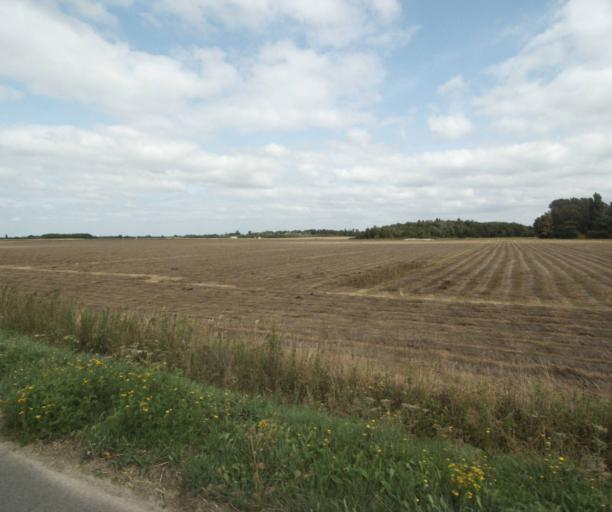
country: FR
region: Nord-Pas-de-Calais
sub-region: Departement du Nord
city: Gruson
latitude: 50.5930
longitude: 3.2289
